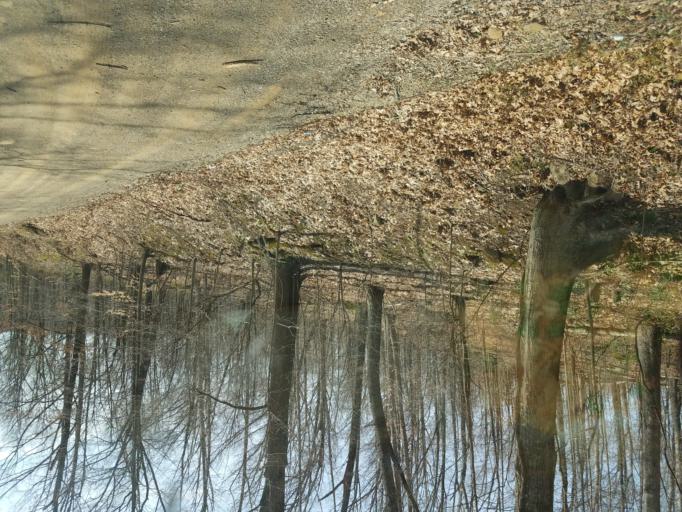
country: US
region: Ohio
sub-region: Knox County
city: Oak Hill
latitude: 40.3799
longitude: -82.1622
